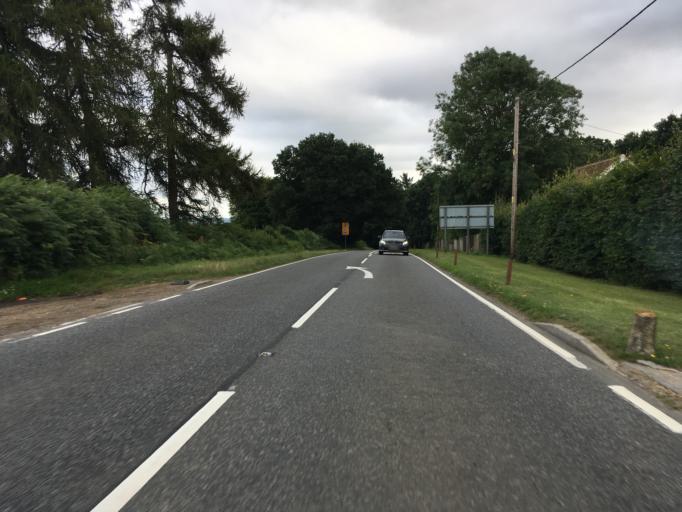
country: GB
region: England
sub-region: Hampshire
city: Petersfield
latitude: 51.0140
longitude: -0.9091
